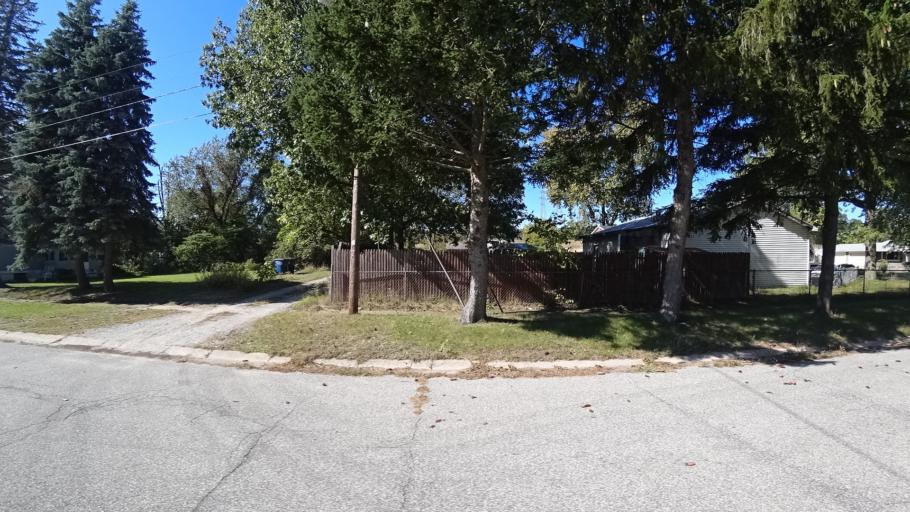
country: US
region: Indiana
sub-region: LaPorte County
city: Michigan City
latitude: 41.7094
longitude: -86.9195
